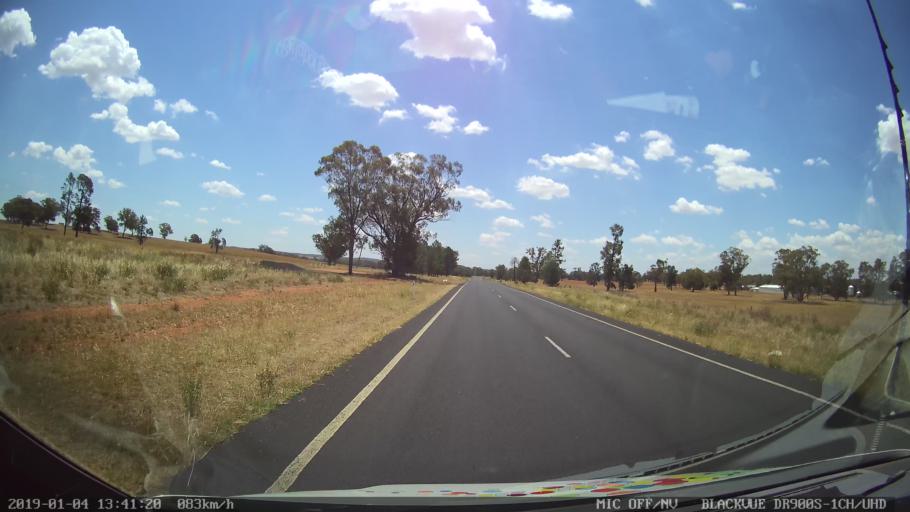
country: AU
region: New South Wales
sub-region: Dubbo Municipality
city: Dubbo
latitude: -32.5036
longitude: 148.5537
